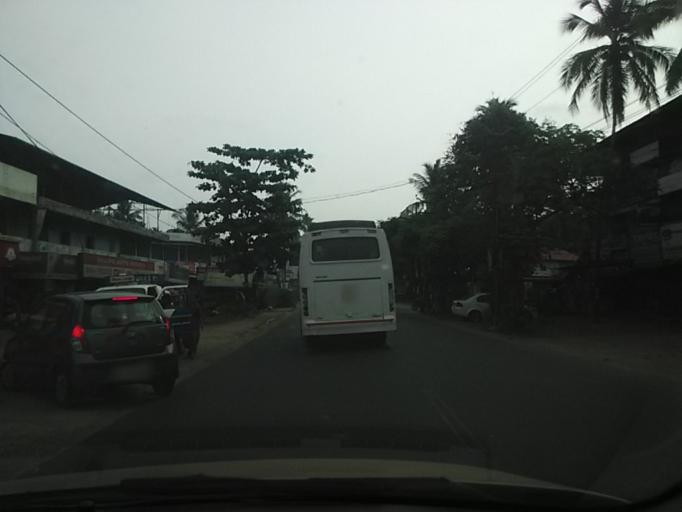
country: IN
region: Kerala
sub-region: Kozhikode
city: Kozhikode
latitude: 11.2760
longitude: 75.7790
